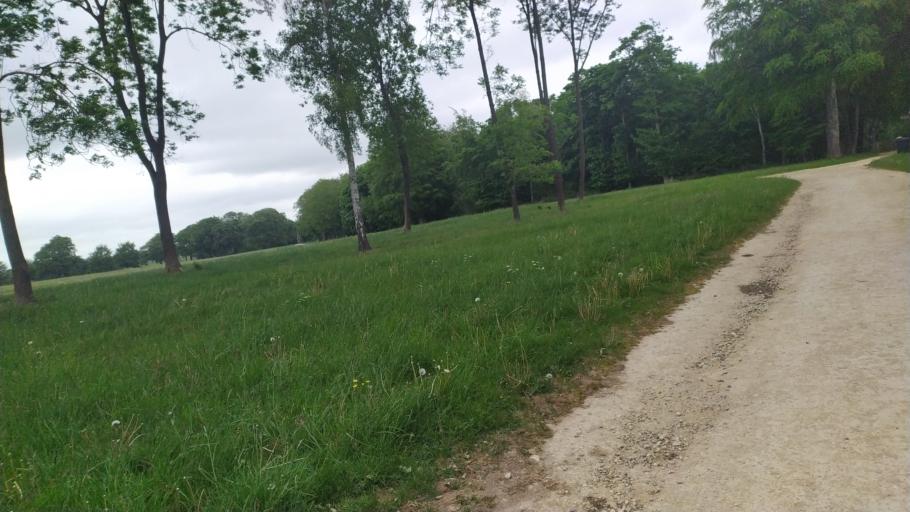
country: GB
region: England
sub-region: City and Borough of Leeds
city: Bramham
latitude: 53.8602
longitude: -1.3785
